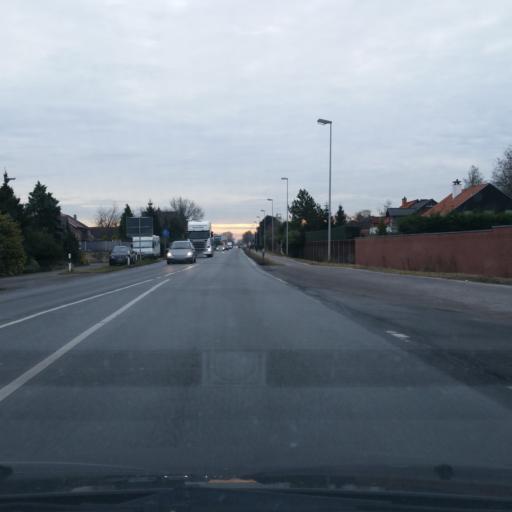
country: DE
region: North Rhine-Westphalia
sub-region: Regierungsbezirk Dusseldorf
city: Bocholt
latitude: 51.8146
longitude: 6.6120
